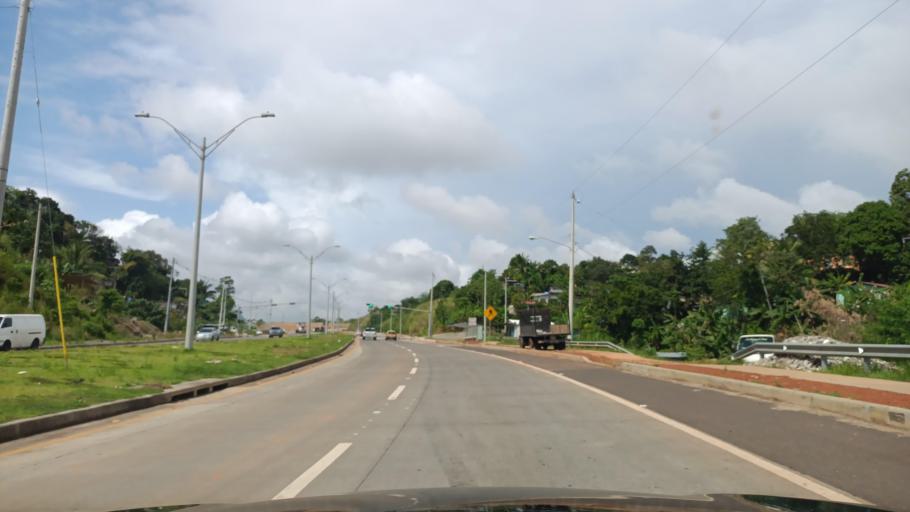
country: PA
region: Panama
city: Las Cumbres
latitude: 9.1021
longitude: -79.4940
